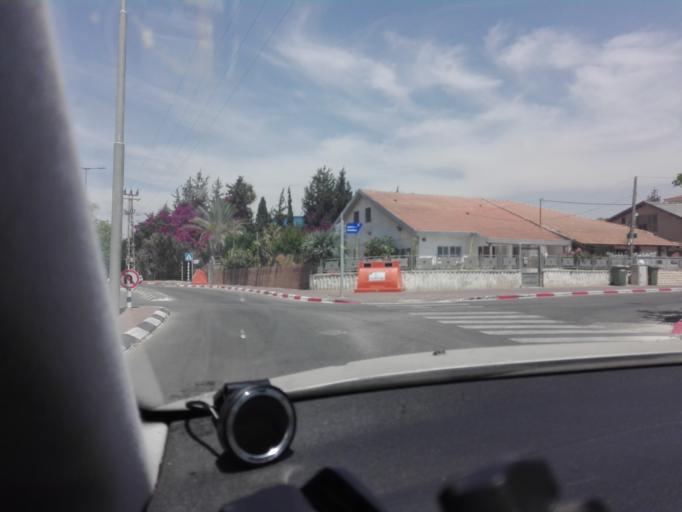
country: IL
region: Central District
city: Bene 'Ayish
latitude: 31.7357
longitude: 34.7510
